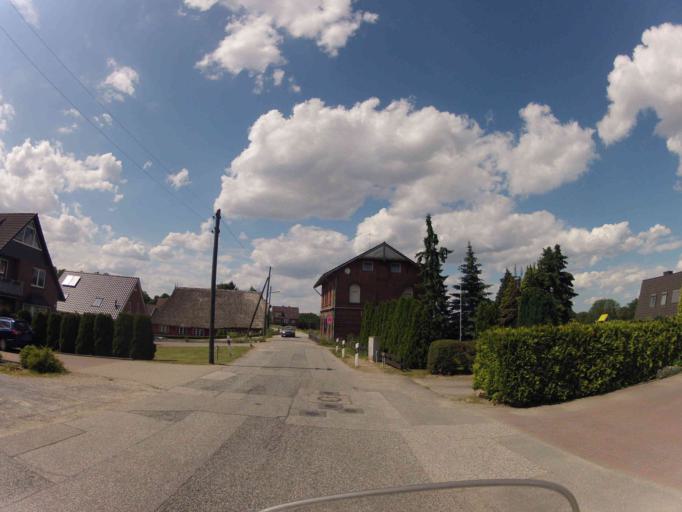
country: DE
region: Hamburg
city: Rothenburgsort
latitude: 53.4952
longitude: 10.0833
